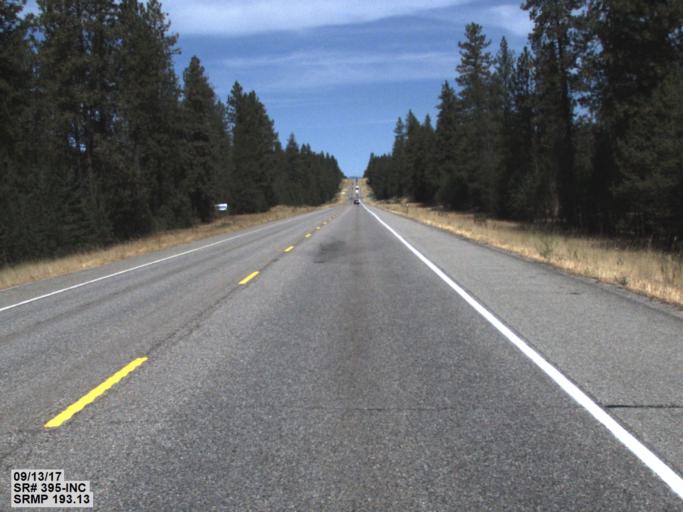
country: US
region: Washington
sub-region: Stevens County
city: Chewelah
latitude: 48.0952
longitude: -117.6372
